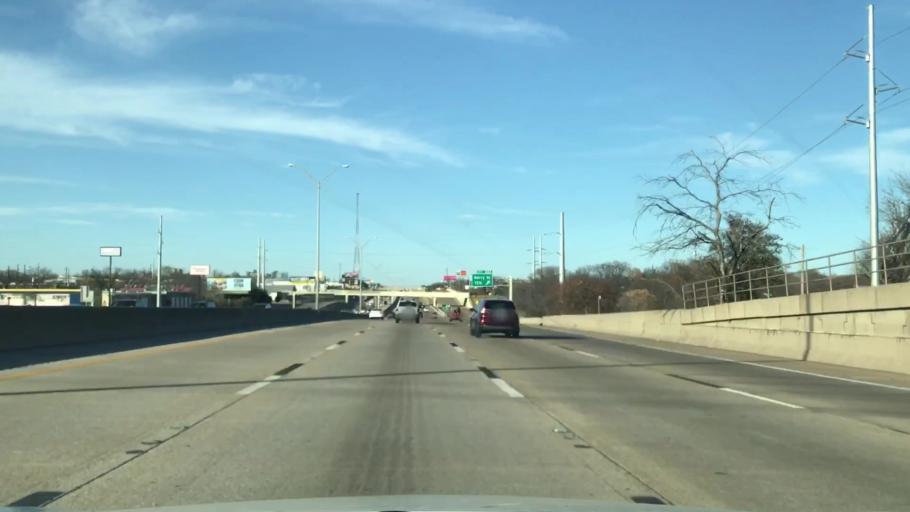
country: US
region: Texas
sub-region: Tarrant County
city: Fort Worth
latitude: 32.6987
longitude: -97.3206
